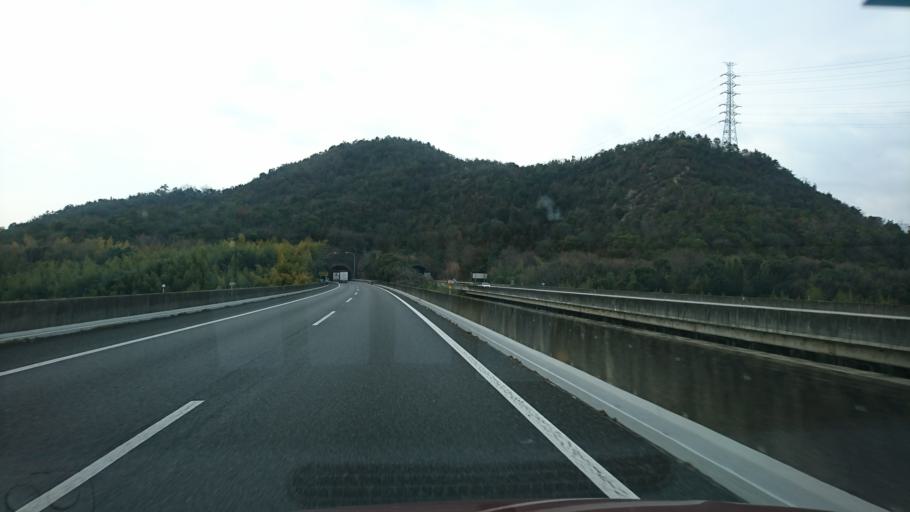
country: JP
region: Okayama
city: Kurashiki
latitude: 34.6202
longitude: 133.7451
